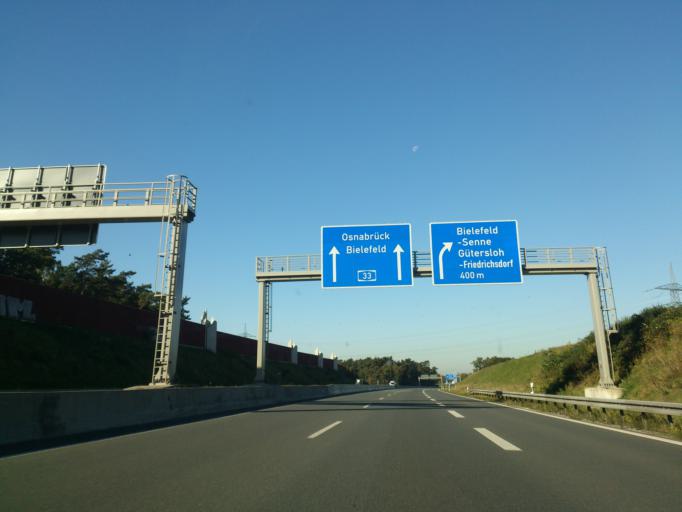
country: DE
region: North Rhine-Westphalia
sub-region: Regierungsbezirk Detmold
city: Verl
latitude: 51.9432
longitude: 8.5307
